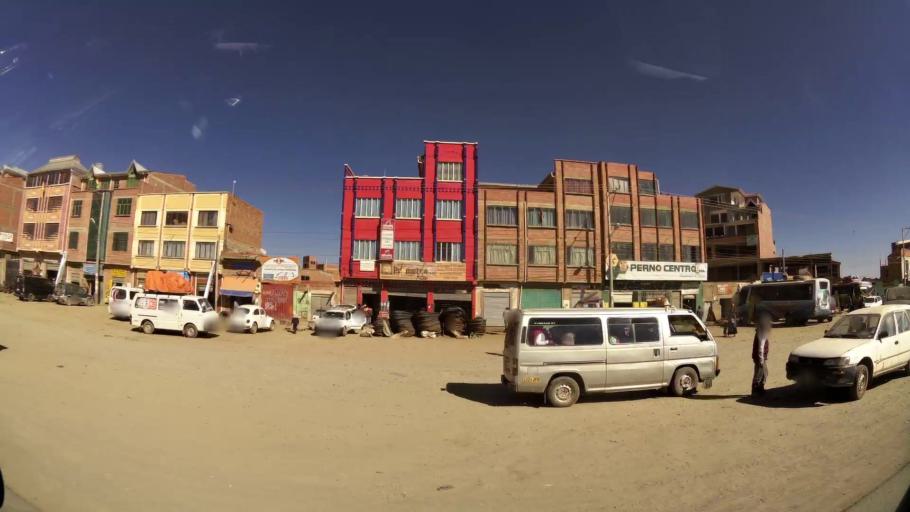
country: BO
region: La Paz
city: La Paz
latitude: -16.5872
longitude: -68.1848
